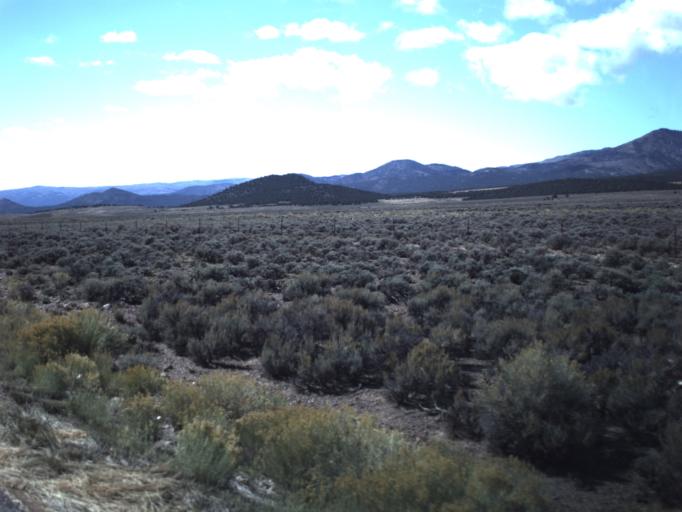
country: US
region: Utah
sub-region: Wayne County
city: Loa
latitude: 38.3704
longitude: -111.9391
